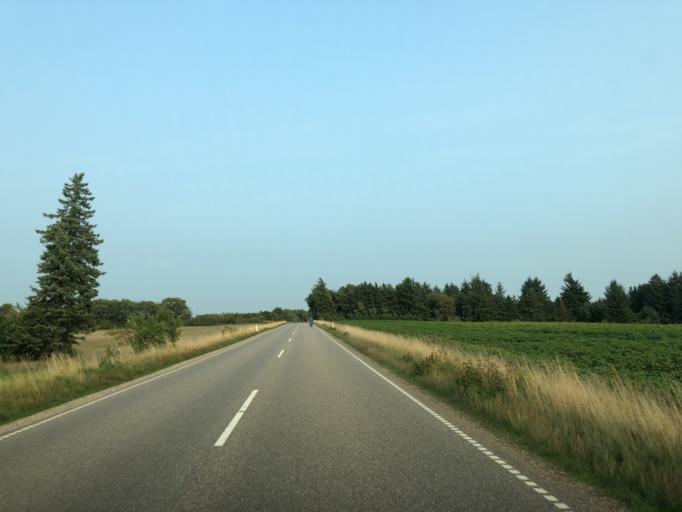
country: DK
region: South Denmark
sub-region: Billund Kommune
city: Grindsted
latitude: 55.8241
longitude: 8.9901
